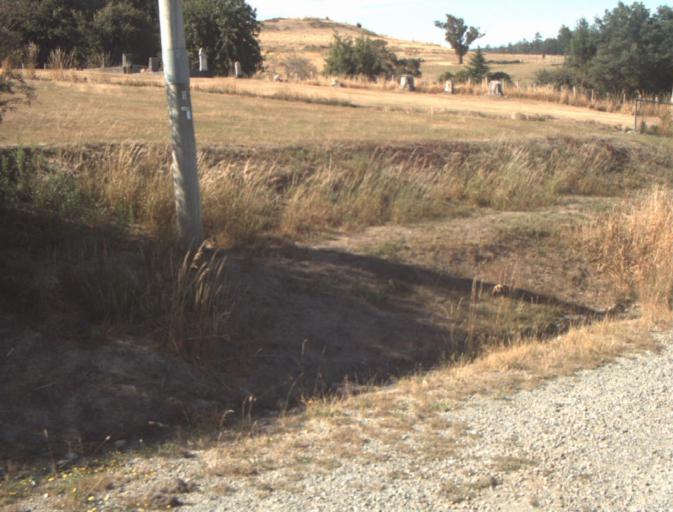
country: AU
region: Tasmania
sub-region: Launceston
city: Mayfield
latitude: -41.1754
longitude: 147.2295
